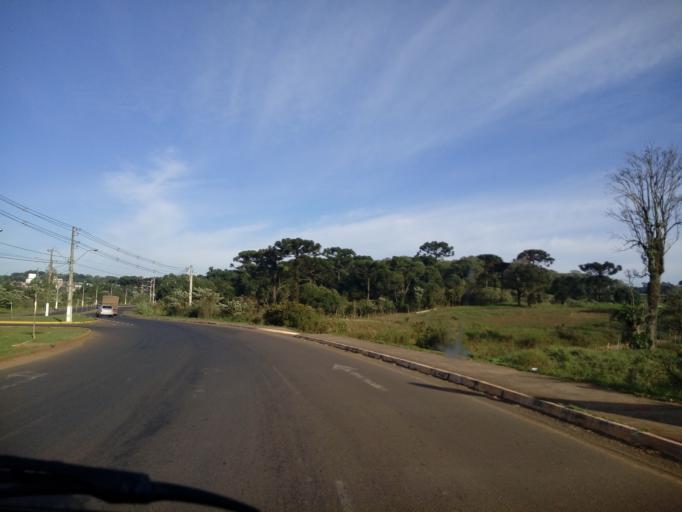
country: BR
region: Santa Catarina
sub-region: Chapeco
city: Chapeco
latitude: -27.0890
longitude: -52.6662
